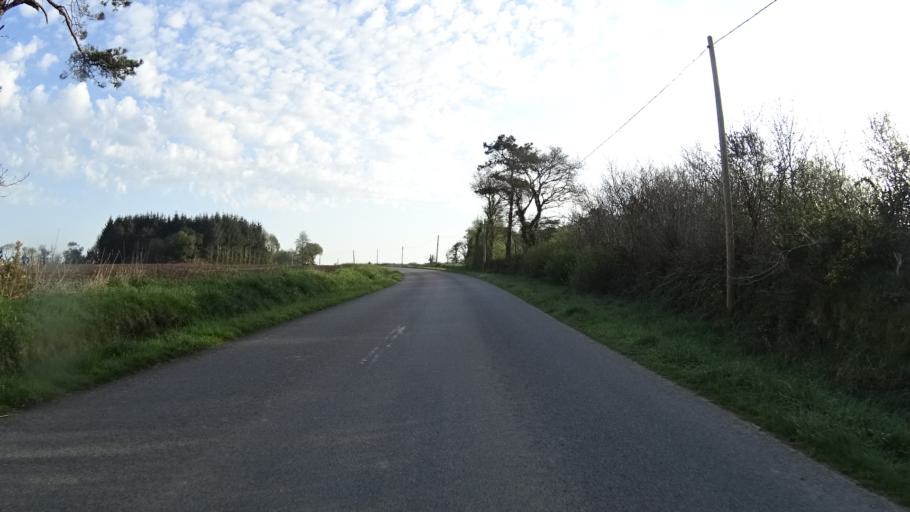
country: FR
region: Brittany
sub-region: Departement du Finistere
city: Sizun
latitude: 48.4269
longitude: -4.0733
